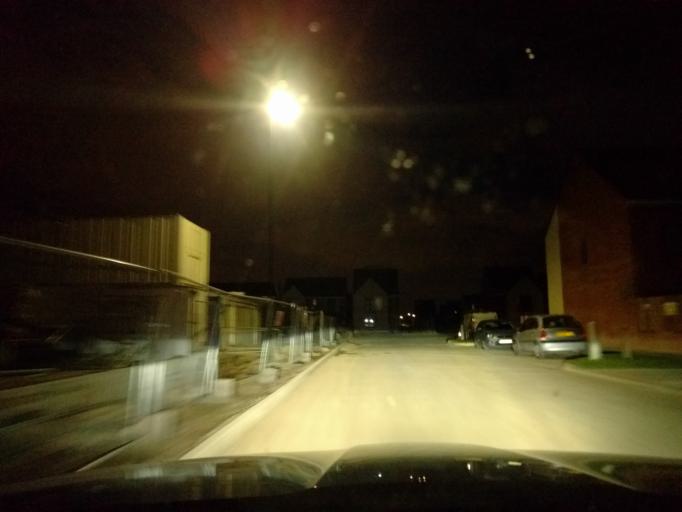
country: GB
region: England
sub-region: Borough of North Tyneside
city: Wallsend
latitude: 55.0117
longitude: -1.5452
